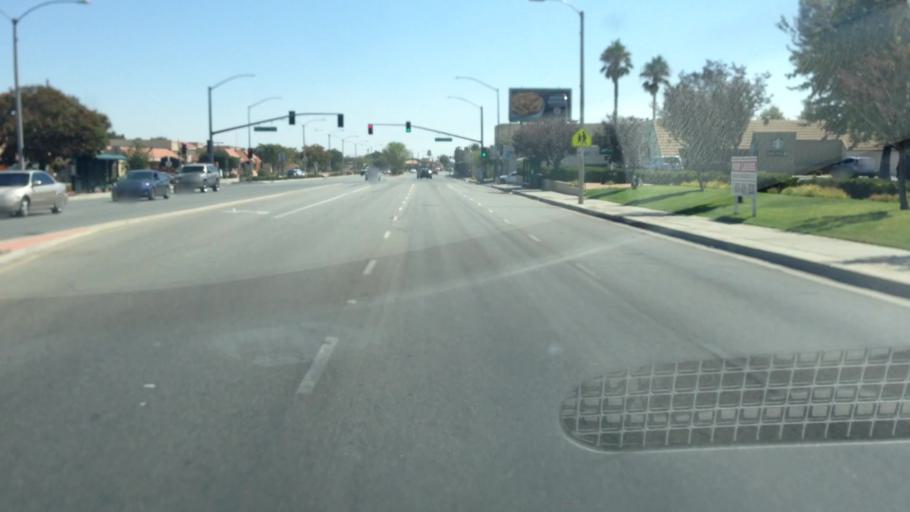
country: US
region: California
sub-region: Los Angeles County
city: Palmdale
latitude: 34.5798
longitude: -118.1260
